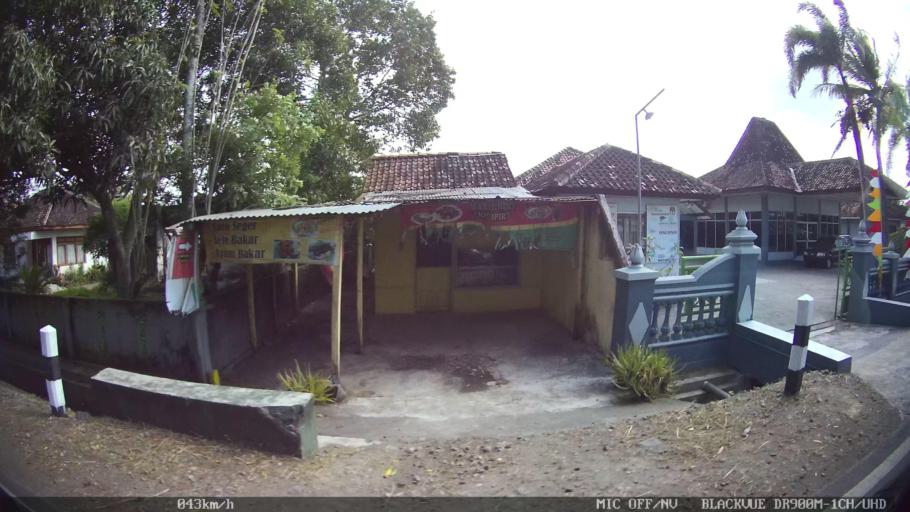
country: ID
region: Daerah Istimewa Yogyakarta
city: Srandakan
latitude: -7.8944
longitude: 110.1473
